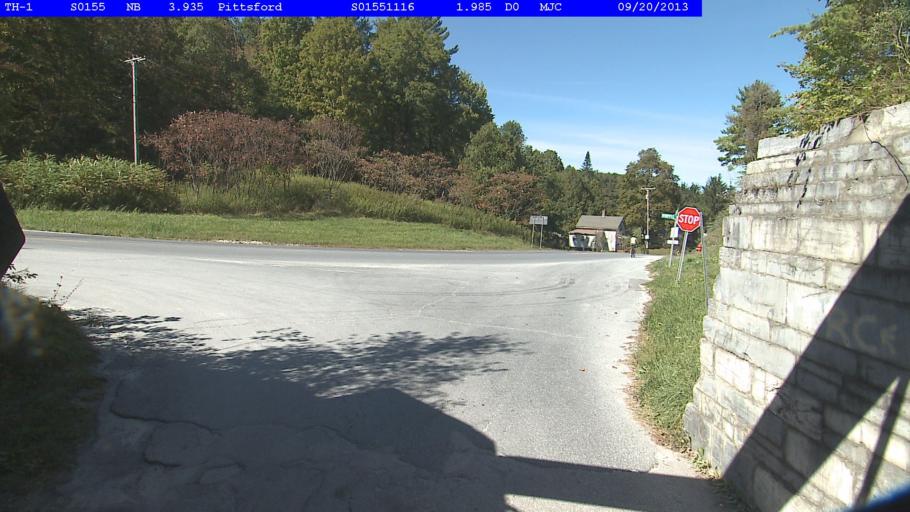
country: US
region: Vermont
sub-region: Rutland County
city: Brandon
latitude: 43.7164
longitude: -73.0605
